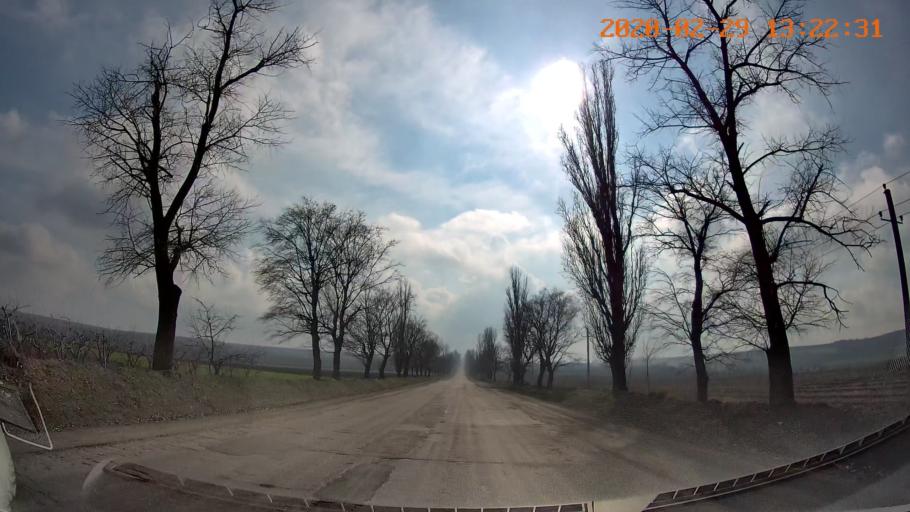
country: MD
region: Telenesti
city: Camenca
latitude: 47.9596
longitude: 28.6277
